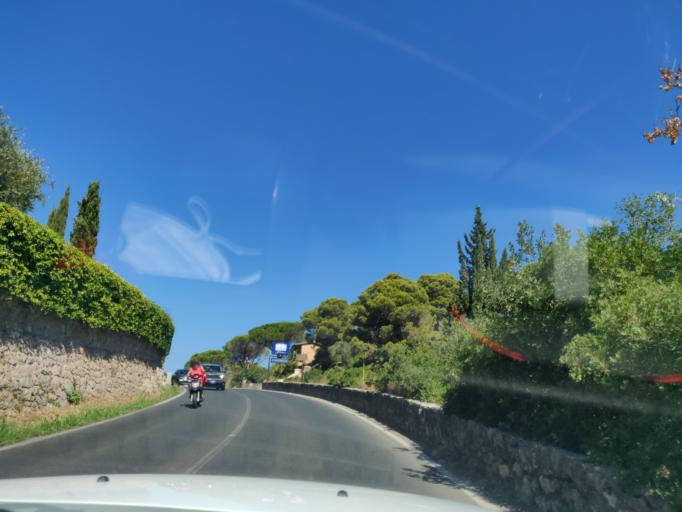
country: IT
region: Tuscany
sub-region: Provincia di Grosseto
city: Monte Argentario
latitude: 42.4352
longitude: 11.1372
